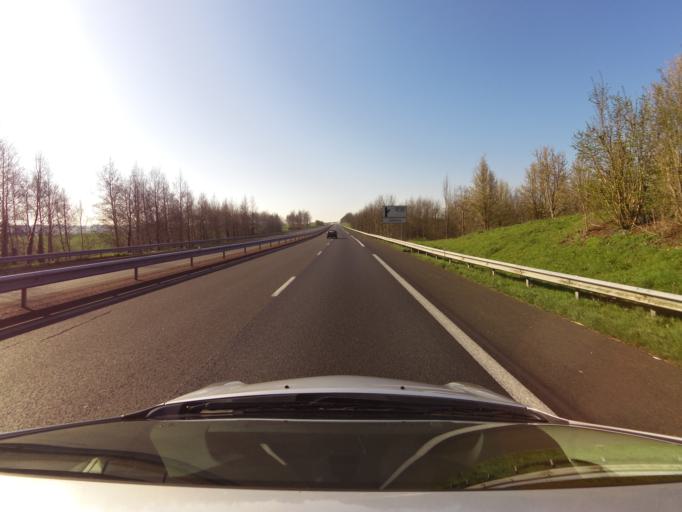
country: FR
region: Lower Normandy
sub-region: Departement de la Manche
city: Saint-James
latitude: 48.5515
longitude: -1.3418
